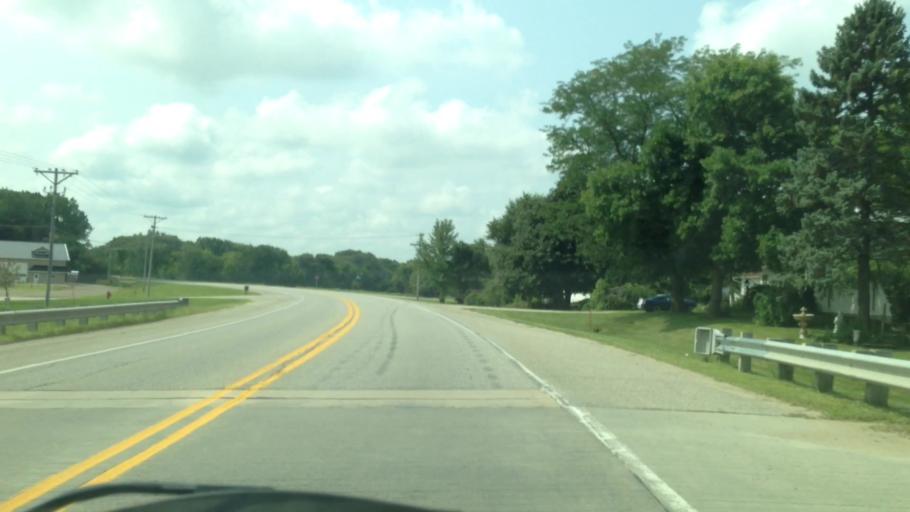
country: US
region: Iowa
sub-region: Linn County
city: Fairfax
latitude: 41.9267
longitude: -91.7830
